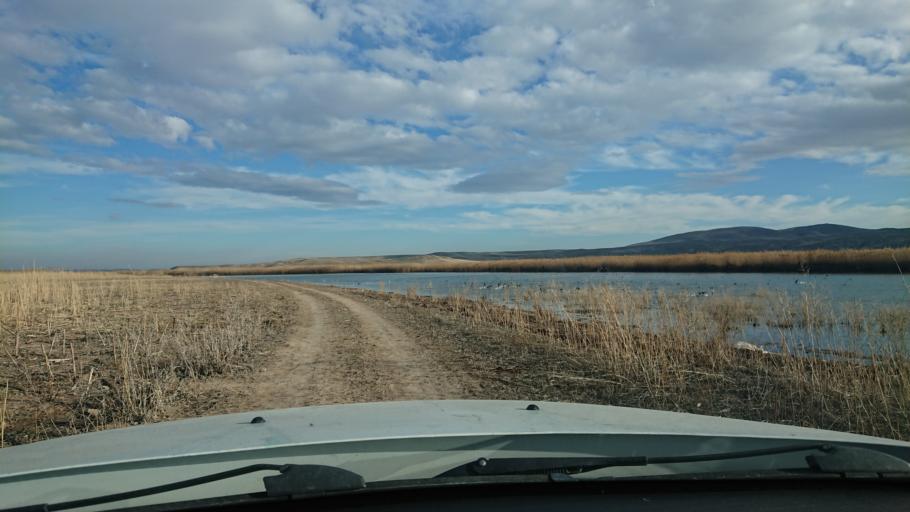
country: TR
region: Aksaray
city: Sariyahsi
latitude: 39.0344
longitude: 33.9614
